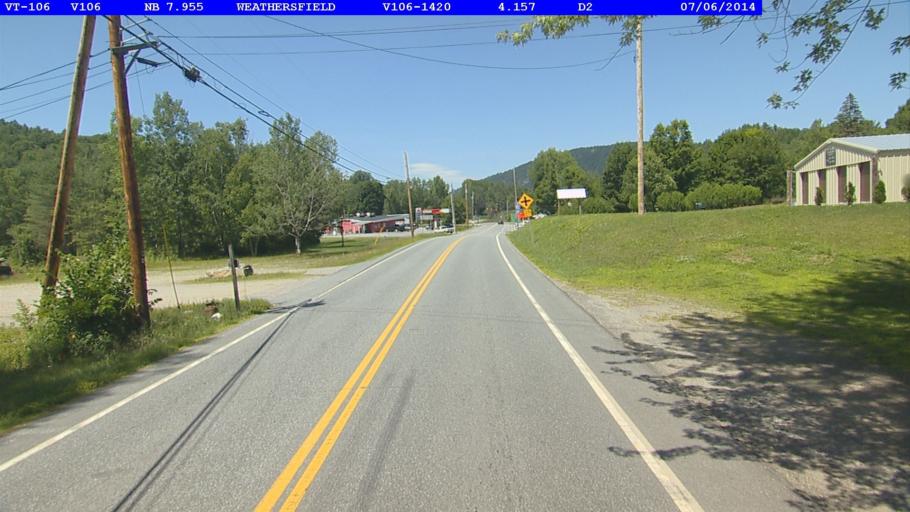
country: US
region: Vermont
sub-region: Windsor County
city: Springfield
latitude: 43.3983
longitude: -72.5147
